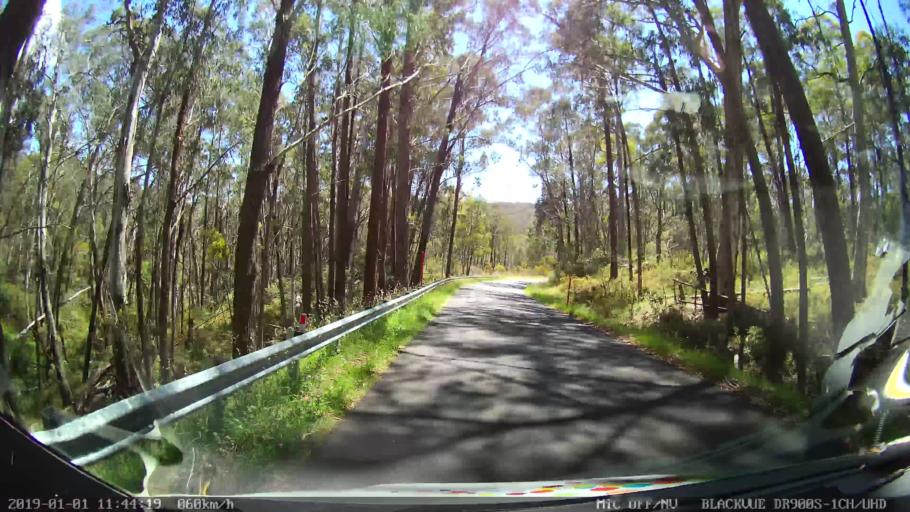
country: AU
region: New South Wales
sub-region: Snowy River
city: Jindabyne
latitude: -35.9009
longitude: 148.3916
